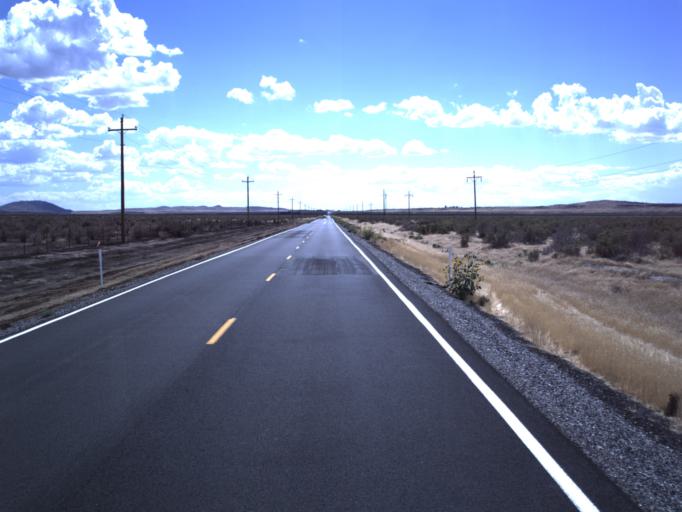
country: US
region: Utah
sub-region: Tooele County
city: Grantsville
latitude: 40.2710
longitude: -112.6810
